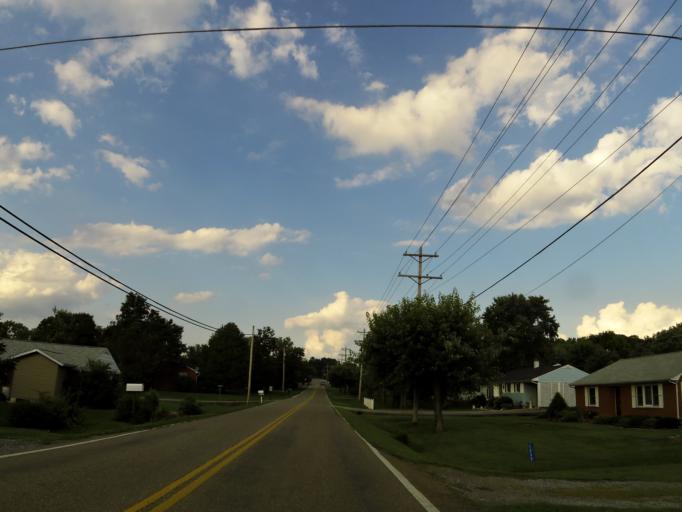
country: US
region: Tennessee
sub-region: Blount County
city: Eagleton Village
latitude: 35.7962
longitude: -83.9491
